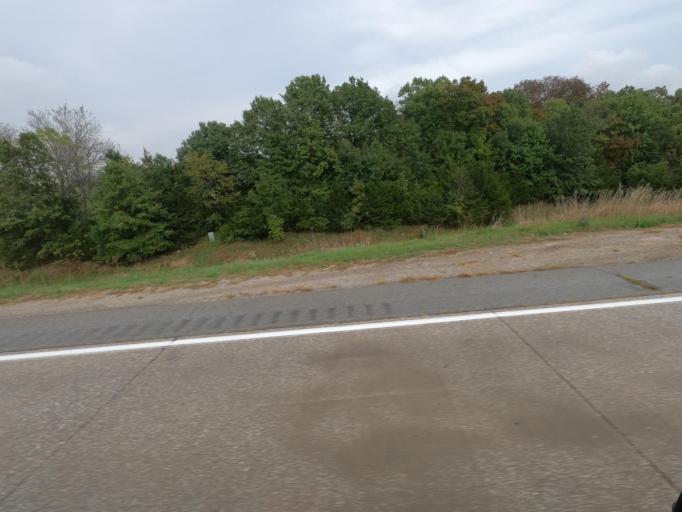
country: US
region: Iowa
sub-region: Van Buren County
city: Keosauqua
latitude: 40.8224
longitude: -91.9470
